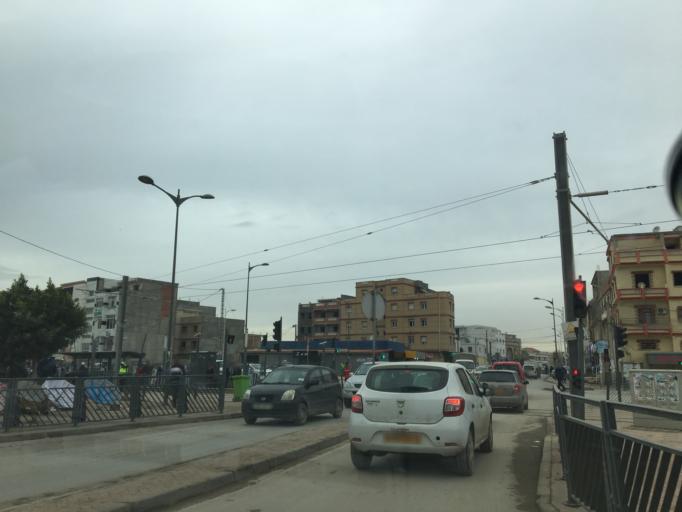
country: DZ
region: Alger
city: Ain Taya
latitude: 36.7773
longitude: 3.2508
